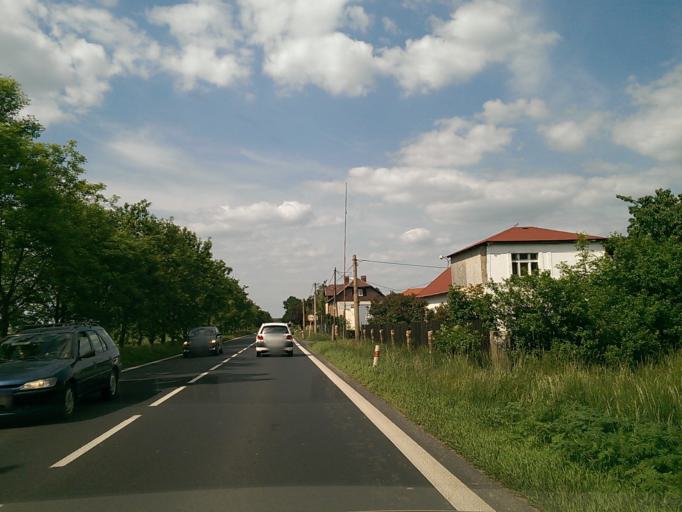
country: CZ
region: Central Bohemia
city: Libis
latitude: 50.2728
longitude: 14.4959
